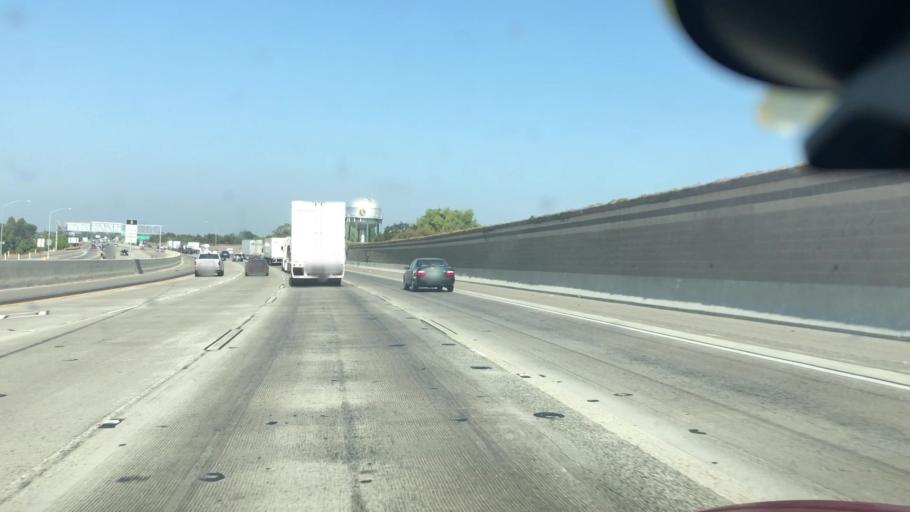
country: US
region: California
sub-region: San Joaquin County
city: Stockton
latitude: 37.9557
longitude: -121.3146
